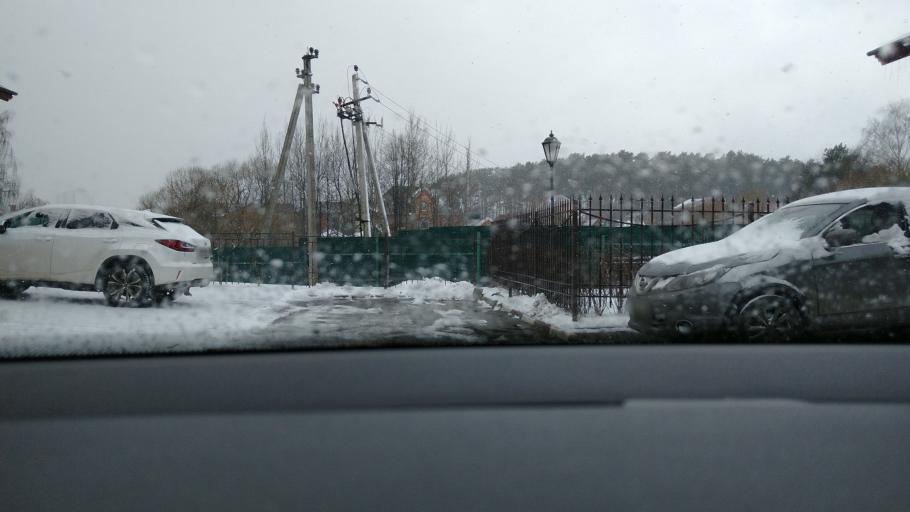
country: RU
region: Moskovskaya
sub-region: Leninskiy Rayon
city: Vnukovo
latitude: 55.6177
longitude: 37.3180
